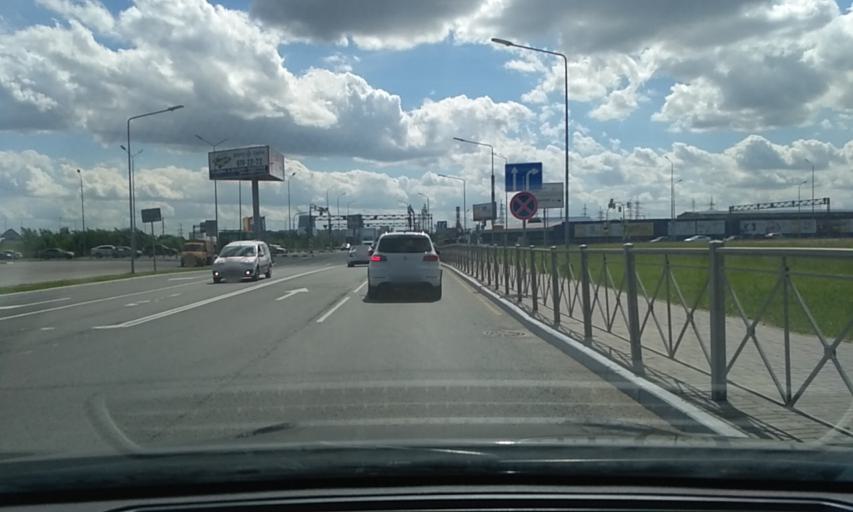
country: RU
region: Leningrad
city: Rybatskoye
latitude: 59.8911
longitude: 30.5085
